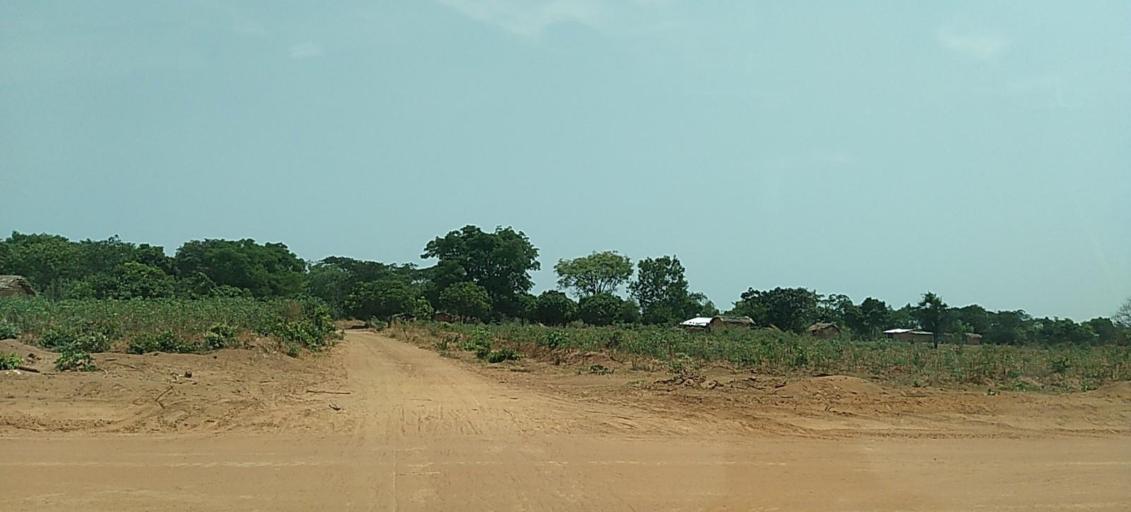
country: ZM
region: Copperbelt
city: Ndola
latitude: -13.0514
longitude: 28.7375
